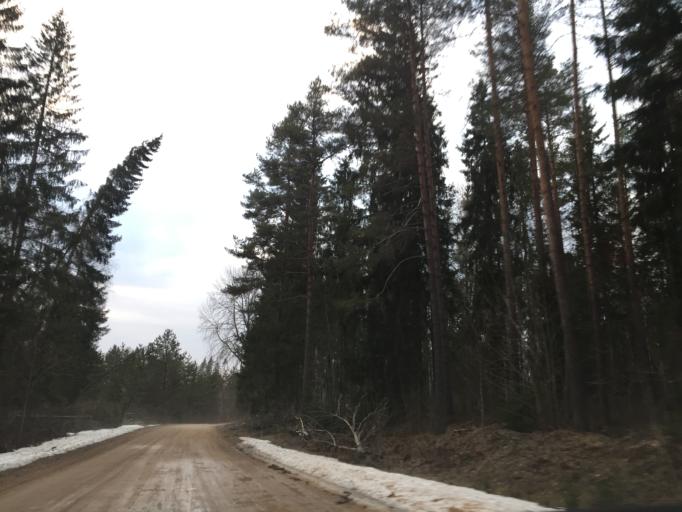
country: LV
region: Vecpiebalga
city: Vecpiebalga
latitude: 57.1352
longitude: 25.6343
